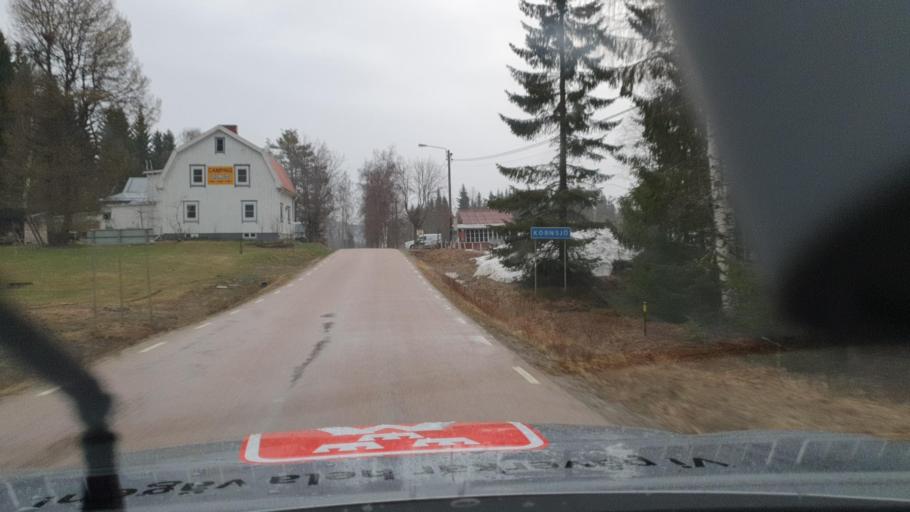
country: SE
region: Vaesternorrland
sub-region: OErnskoeldsviks Kommun
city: Bjasta
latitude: 63.2027
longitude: 18.4166
